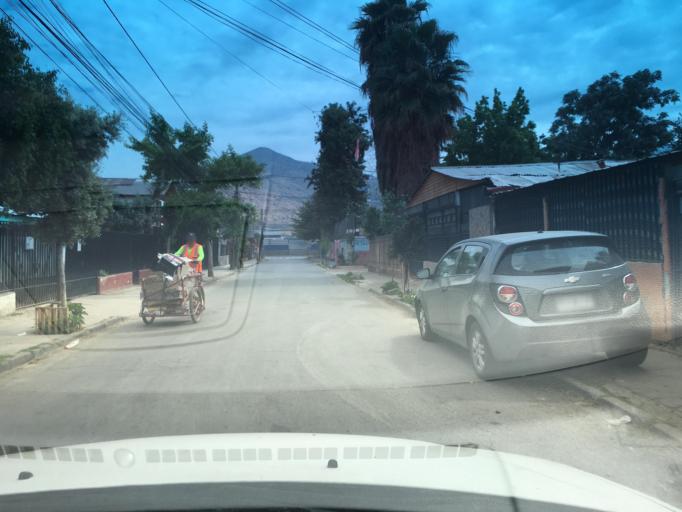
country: CL
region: Santiago Metropolitan
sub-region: Provincia de Santiago
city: Santiago
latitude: -33.3823
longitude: -70.6447
